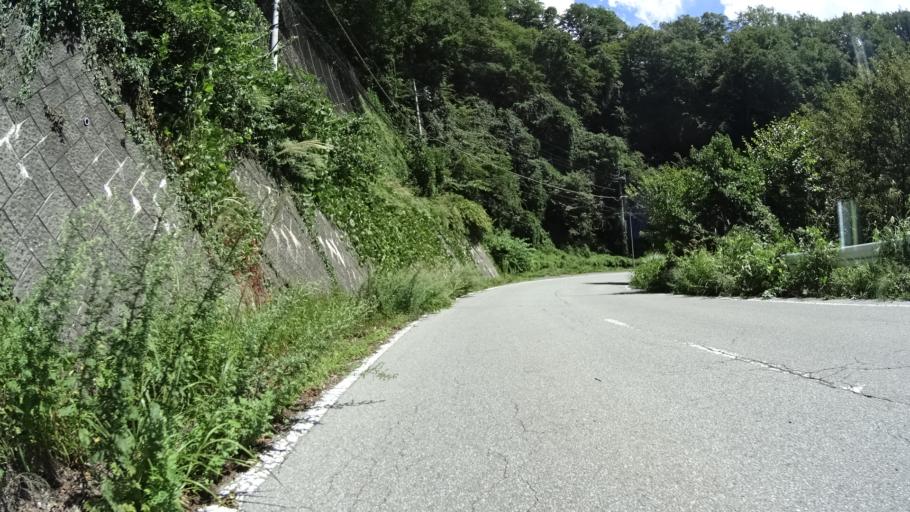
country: JP
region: Yamanashi
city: Enzan
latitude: 35.6578
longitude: 138.8158
